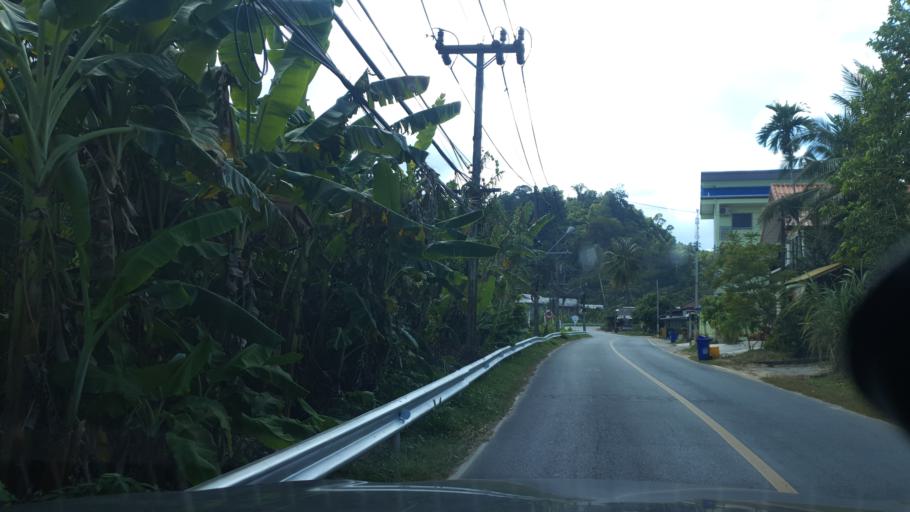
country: TH
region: Phuket
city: Thalang
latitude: 8.0668
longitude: 98.2924
